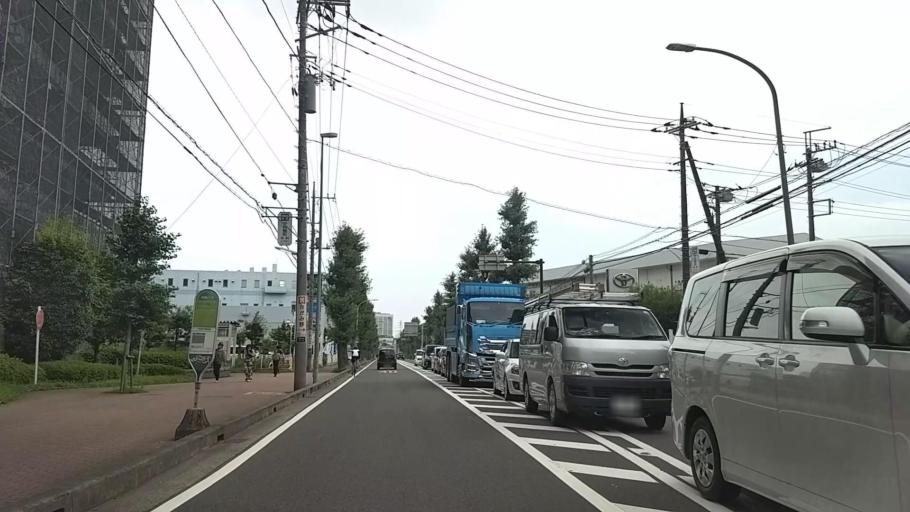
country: JP
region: Kanagawa
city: Minami-rinkan
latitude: 35.4707
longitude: 139.4301
